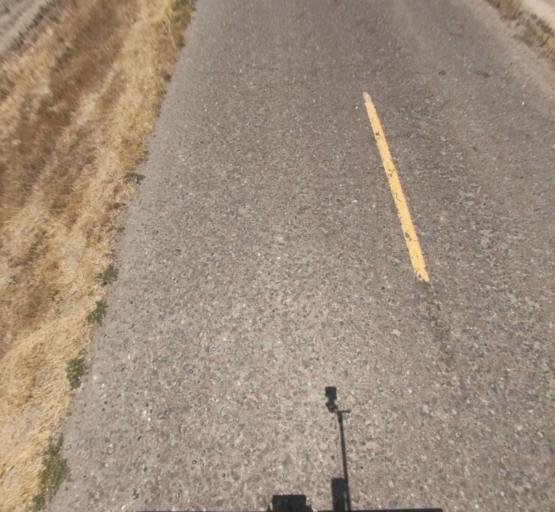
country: US
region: California
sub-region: Fresno County
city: Biola
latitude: 36.8222
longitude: -120.1278
